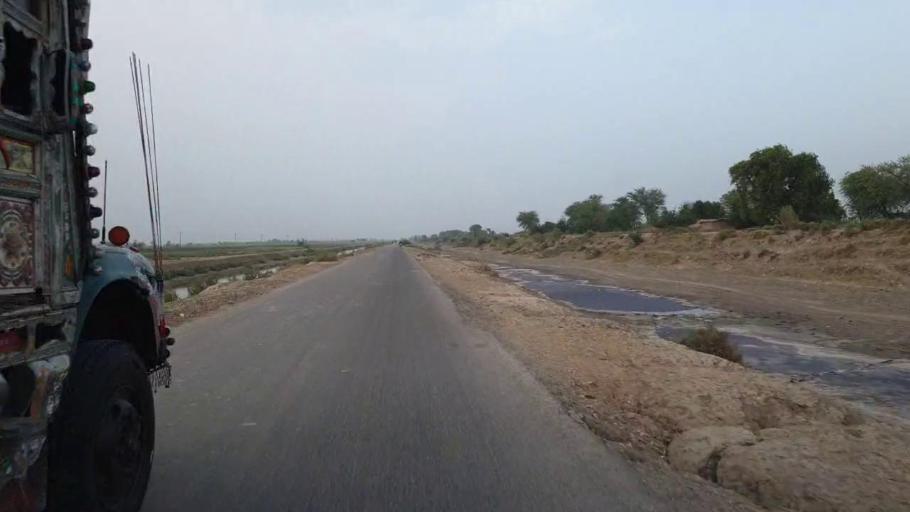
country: PK
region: Sindh
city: Daur
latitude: 26.4406
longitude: 68.2771
